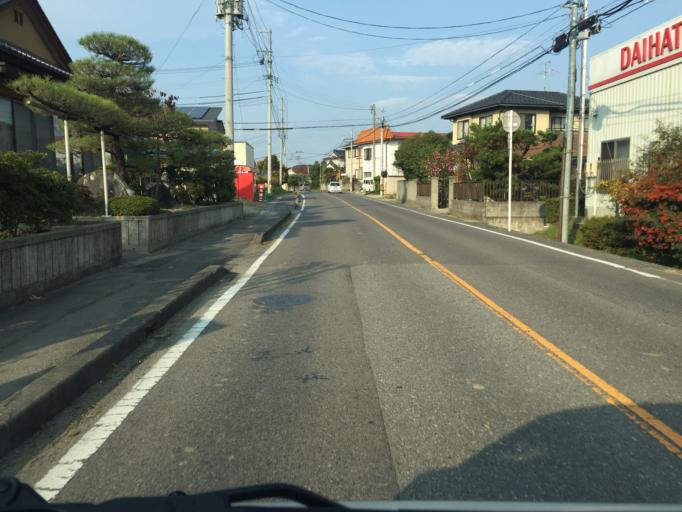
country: JP
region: Fukushima
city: Motomiya
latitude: 37.4963
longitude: 140.4023
